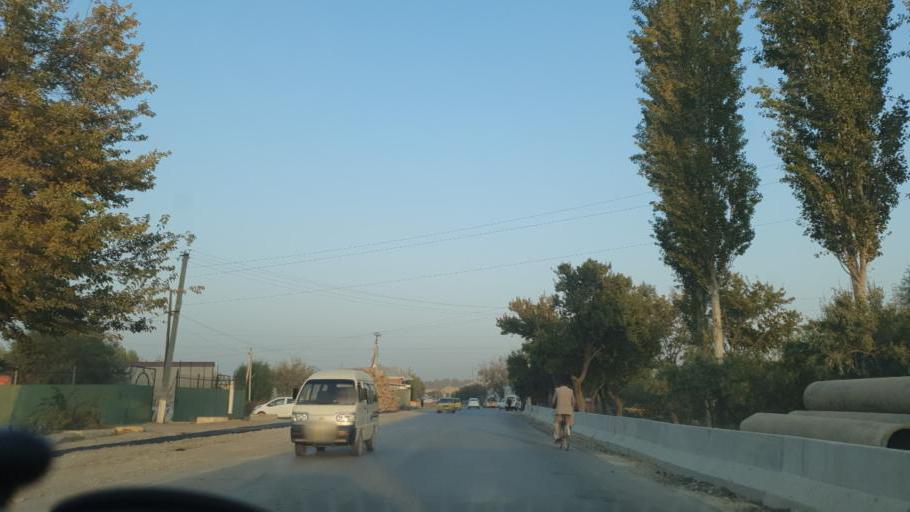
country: UZ
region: Fergana
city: Yaypan
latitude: 40.3782
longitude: 70.7994
